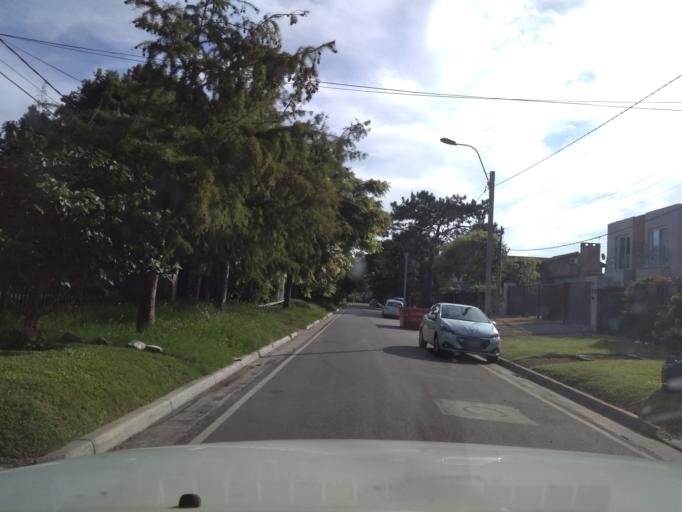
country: UY
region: Canelones
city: Barra de Carrasco
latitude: -34.8702
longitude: -56.0369
